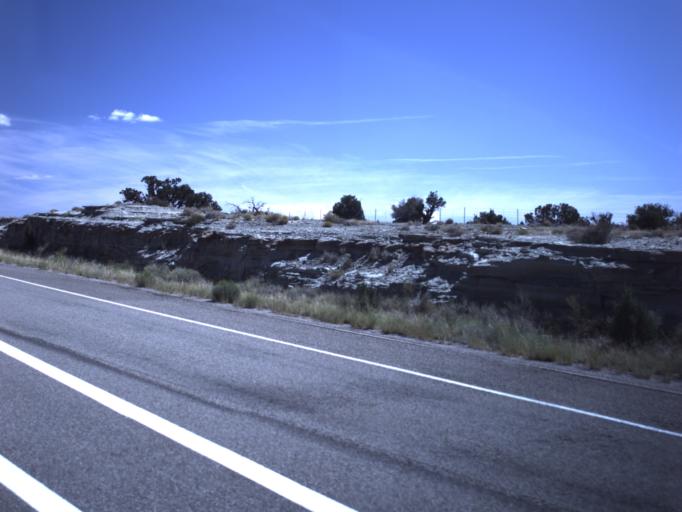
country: US
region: Utah
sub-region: Emery County
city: Ferron
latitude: 38.8307
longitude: -111.1231
